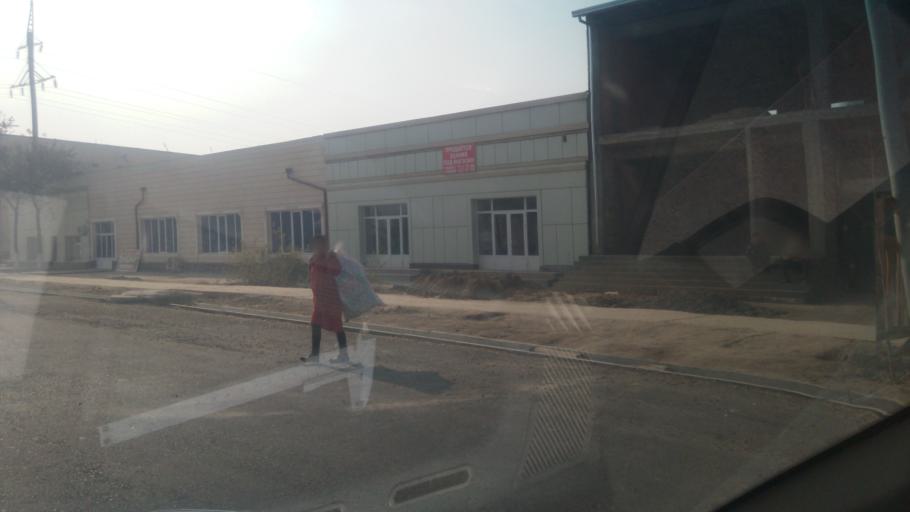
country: UZ
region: Sirdaryo
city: Guliston
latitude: 40.5055
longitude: 68.7742
